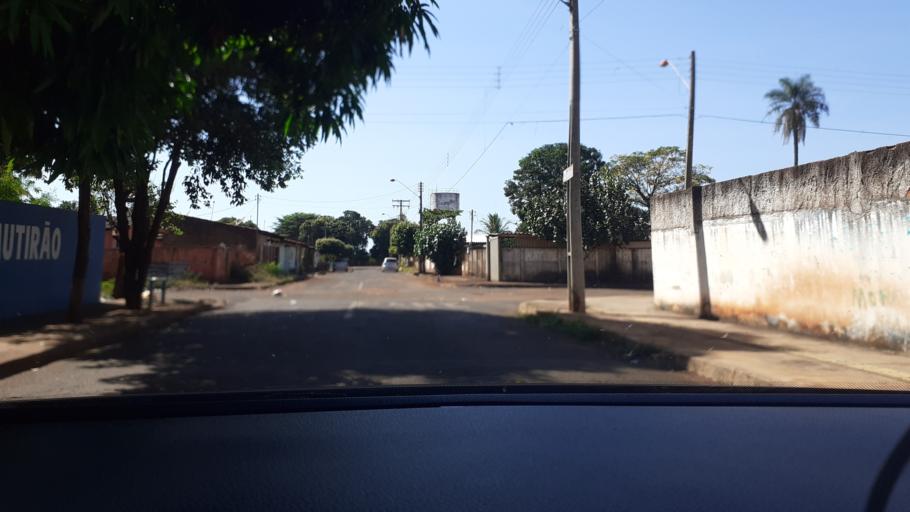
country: BR
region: Goias
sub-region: Itumbiara
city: Itumbiara
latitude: -18.4116
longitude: -49.2555
